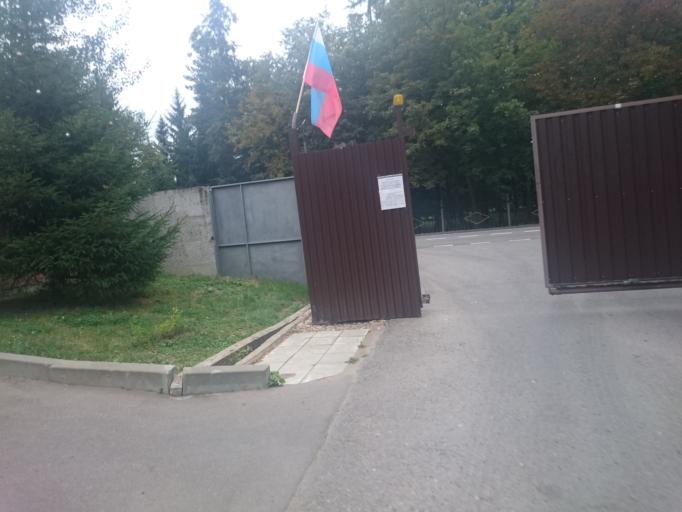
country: RU
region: Moskovskaya
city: Novopodrezkovo
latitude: 55.8938
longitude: 37.3607
